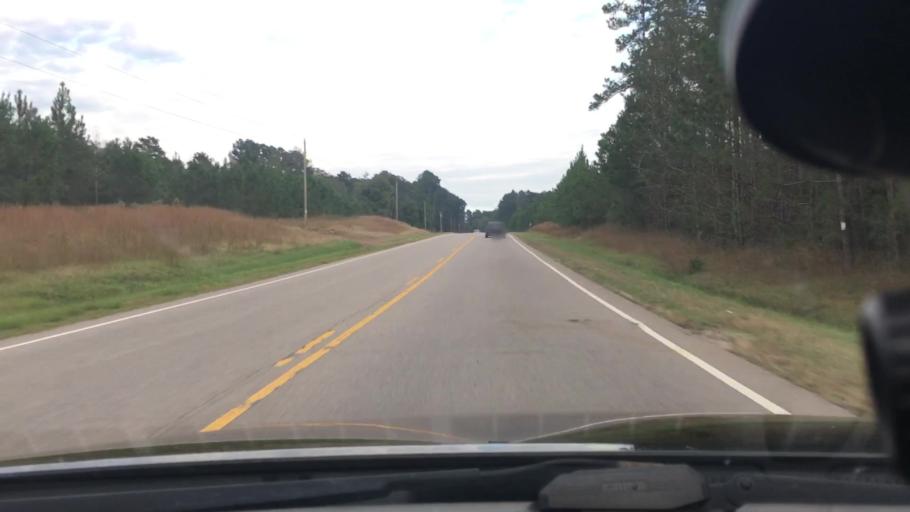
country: US
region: North Carolina
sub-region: Moore County
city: Carthage
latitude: 35.3822
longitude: -79.4829
